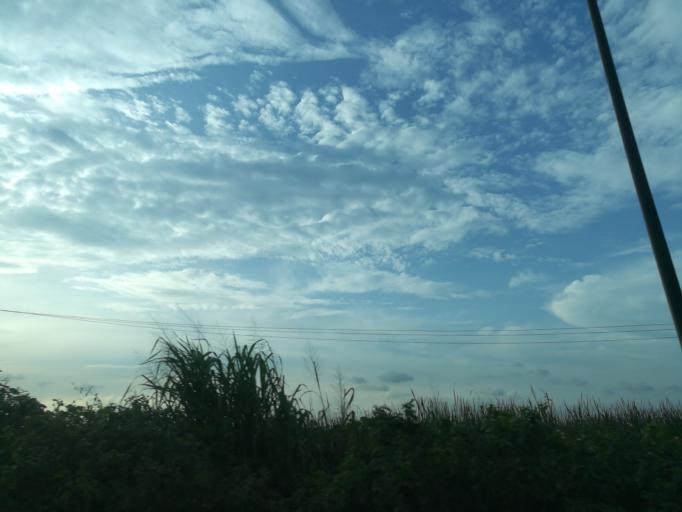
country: NG
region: Lagos
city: Ebute Ikorodu
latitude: 6.6197
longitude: 3.4495
